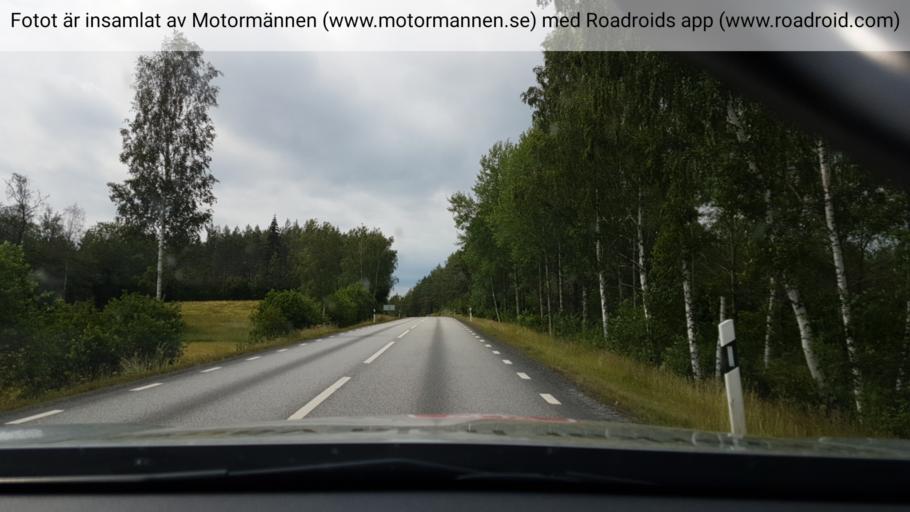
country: SE
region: Joenkoeping
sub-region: Mullsjo Kommun
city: Mullsjoe
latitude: 57.9304
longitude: 13.9298
